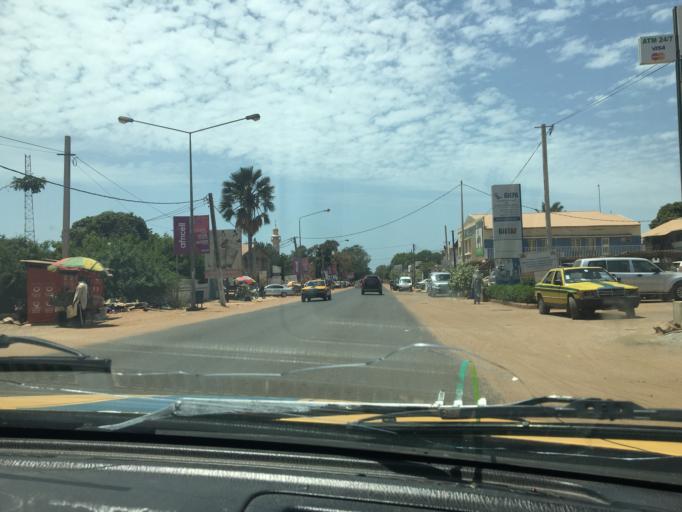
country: GM
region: Banjul
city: Bakau
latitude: 13.4559
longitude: -16.6830
